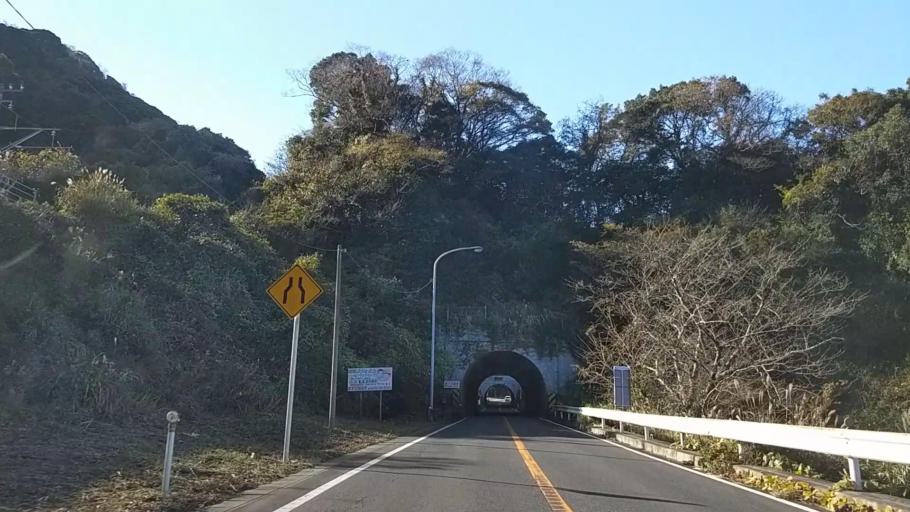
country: JP
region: Chiba
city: Tateyama
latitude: 35.0778
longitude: 139.8390
